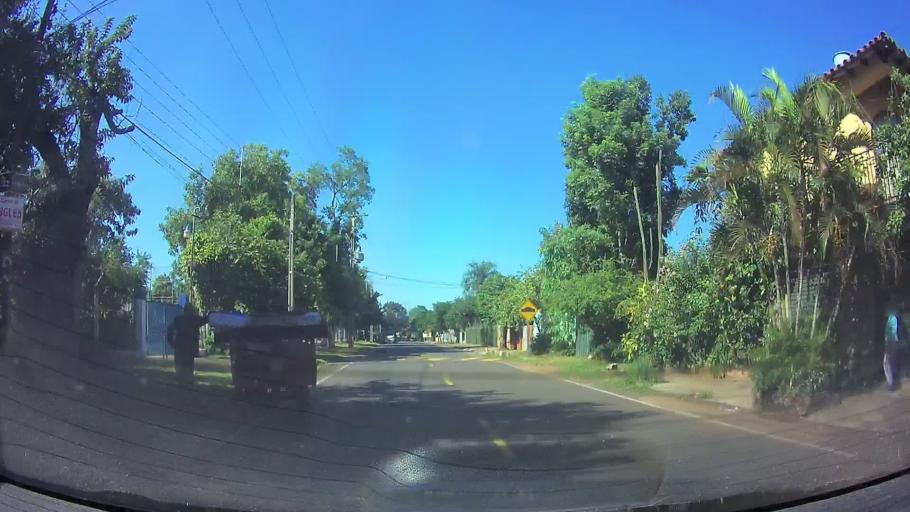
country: PY
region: Central
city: San Lorenzo
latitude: -25.2764
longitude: -57.5050
